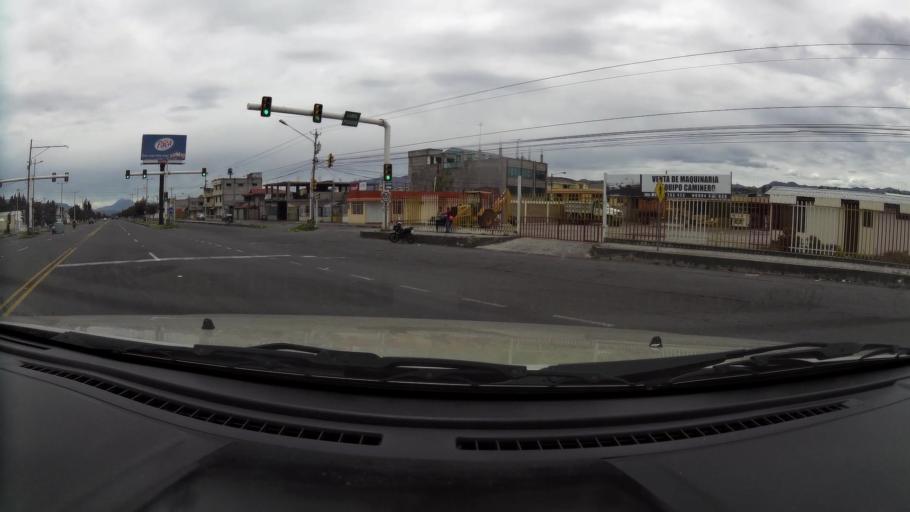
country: EC
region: Cotopaxi
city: Latacunga
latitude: -0.9674
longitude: -78.6122
